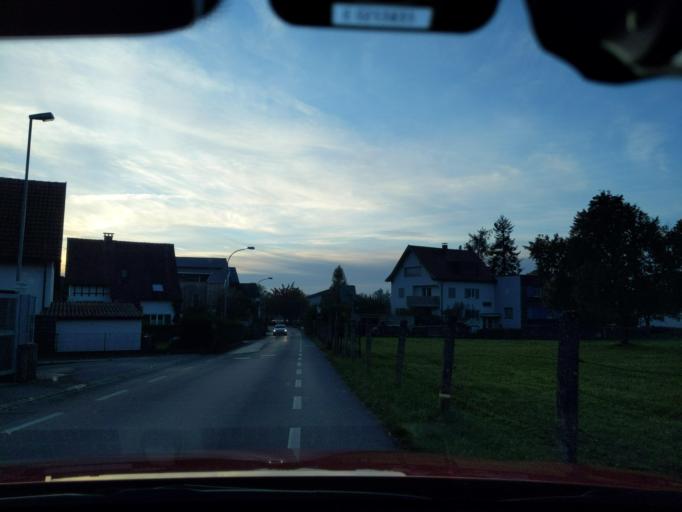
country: AT
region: Vorarlberg
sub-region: Politischer Bezirk Bregenz
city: Lochau
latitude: 47.5342
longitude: 9.7490
